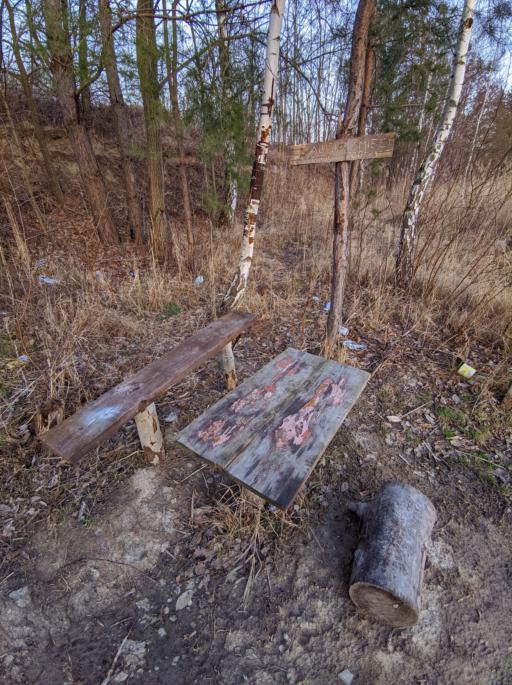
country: PL
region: Lubusz
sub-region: Powiat zarski
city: Tuplice
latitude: 51.6576
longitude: 14.8311
